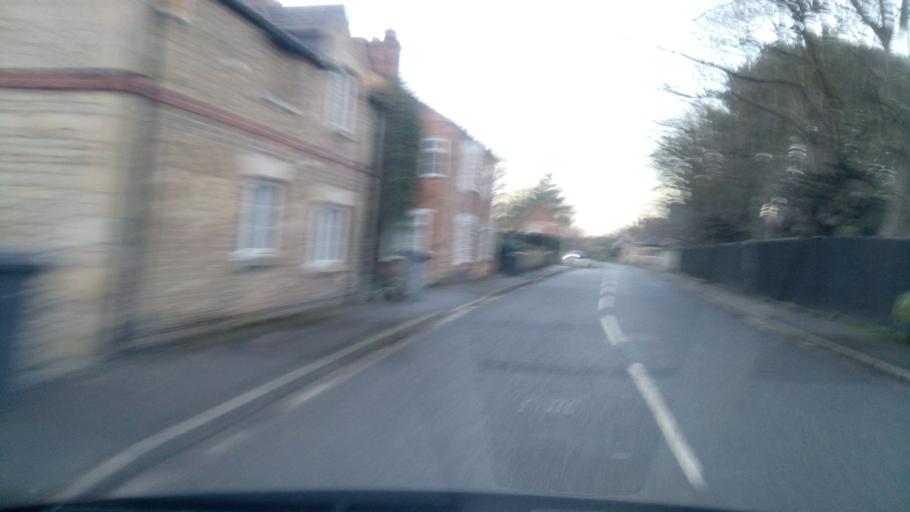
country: GB
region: England
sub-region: Peterborough
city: Castor
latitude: 52.5727
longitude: -0.3455
